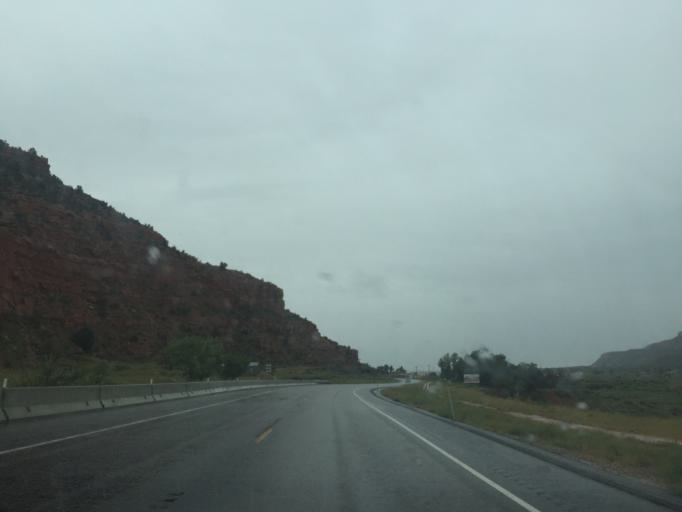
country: US
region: Utah
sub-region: Kane County
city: Kanab
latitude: 37.0638
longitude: -112.5370
